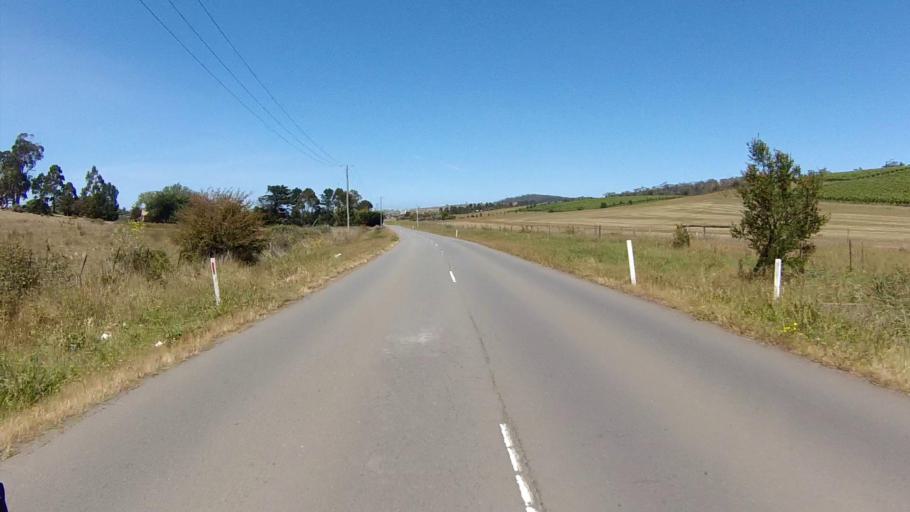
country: AU
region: Tasmania
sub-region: Clarence
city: Howrah
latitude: -42.8733
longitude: 147.4256
